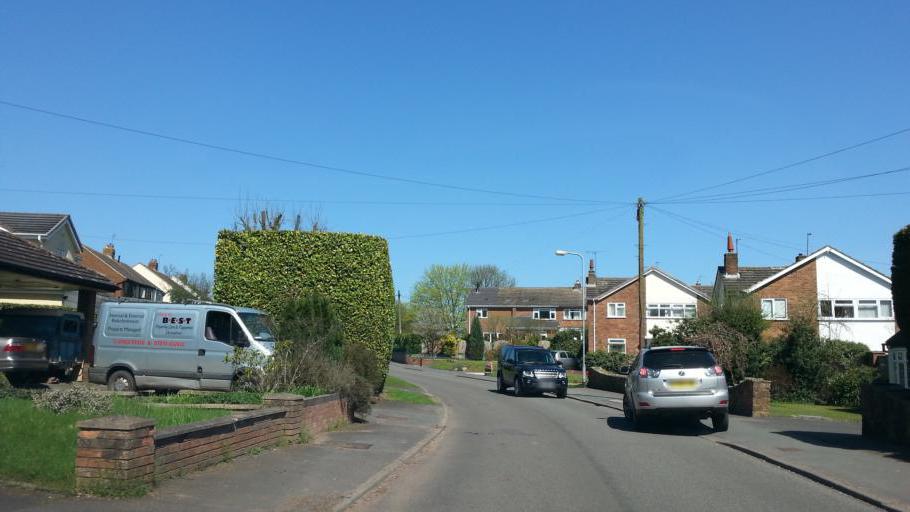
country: GB
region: England
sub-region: Staffordshire
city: Brewood
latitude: 52.6767
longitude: -2.1704
